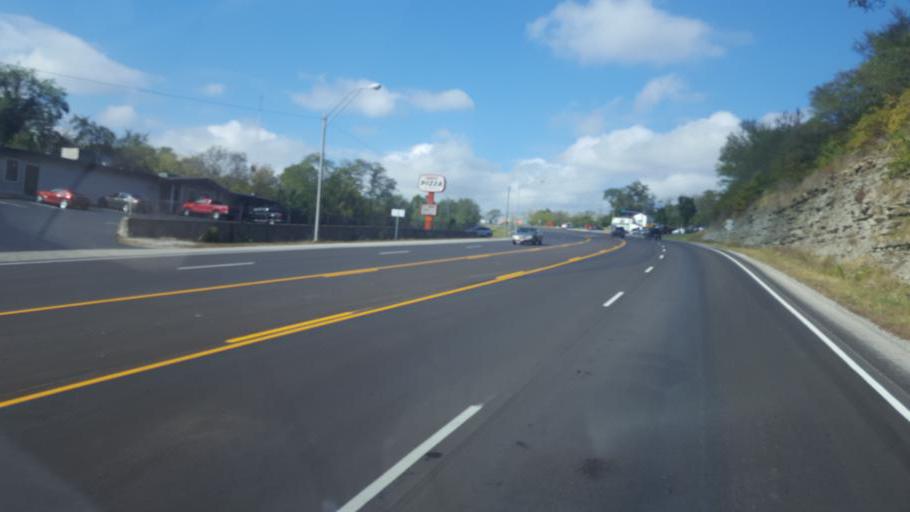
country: US
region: Ohio
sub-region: Brown County
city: Aberdeen
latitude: 38.6439
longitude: -83.7753
